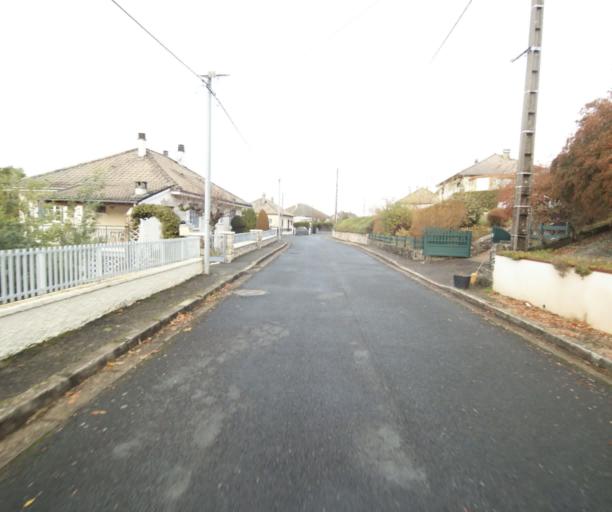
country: FR
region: Limousin
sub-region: Departement de la Correze
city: Cornil
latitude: 45.2073
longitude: 1.6950
